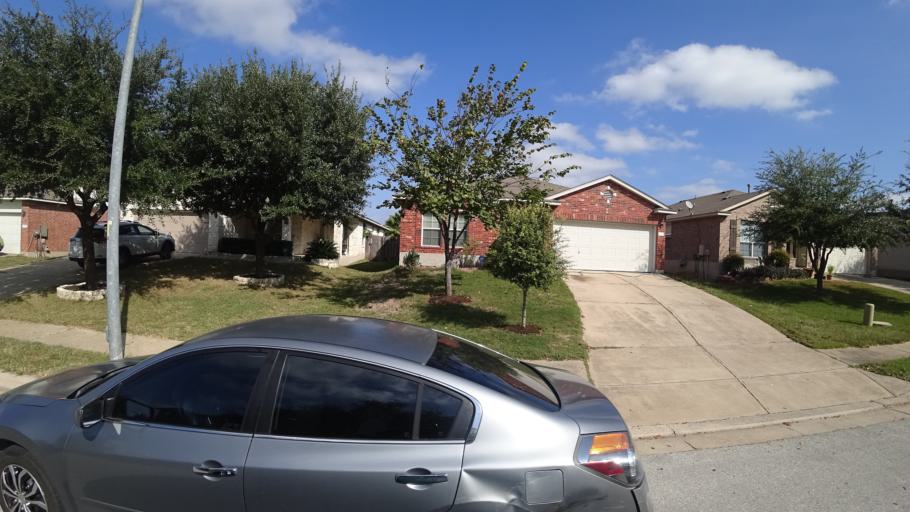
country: US
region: Texas
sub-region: Travis County
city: Pflugerville
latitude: 30.4238
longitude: -97.6410
